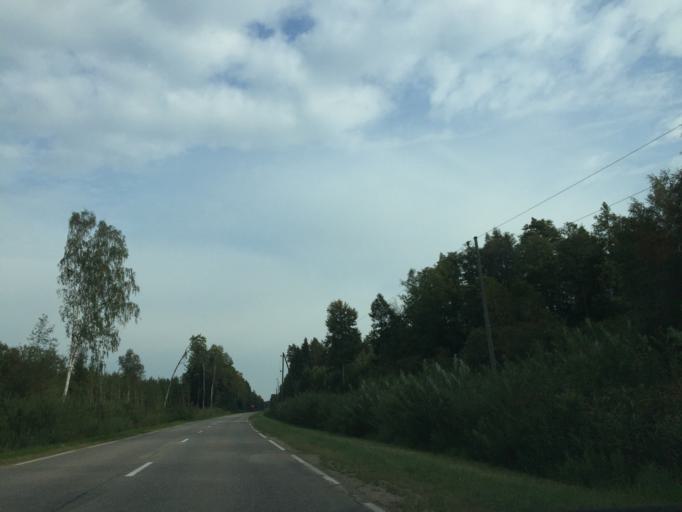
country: LV
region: Ikskile
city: Ikskile
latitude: 56.8159
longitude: 24.4705
